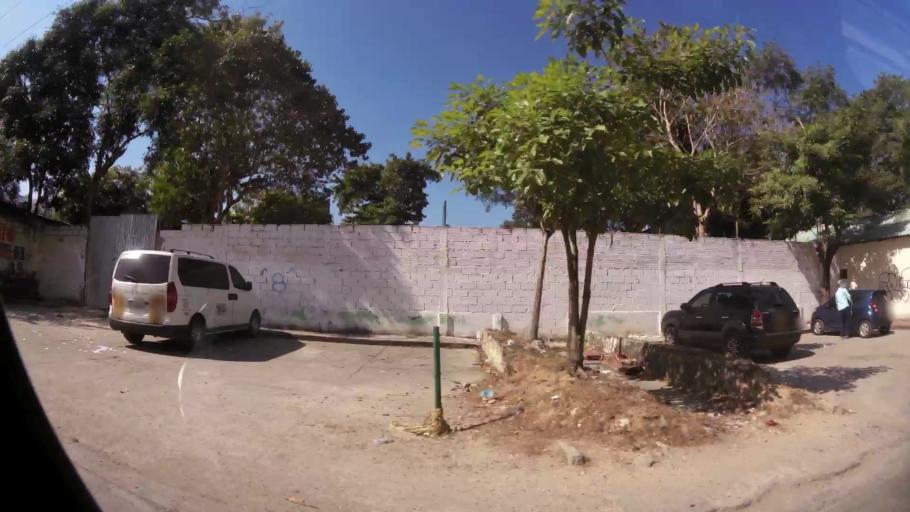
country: CO
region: Bolivar
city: Cartagena
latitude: 10.3903
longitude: -75.4692
